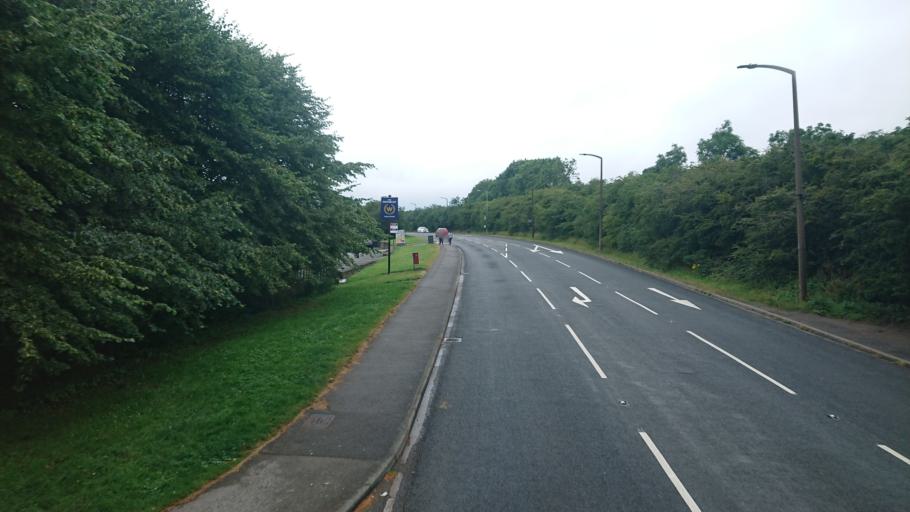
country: GB
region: England
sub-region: Rotherham
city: Catcliffe
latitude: 53.3970
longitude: -1.3697
